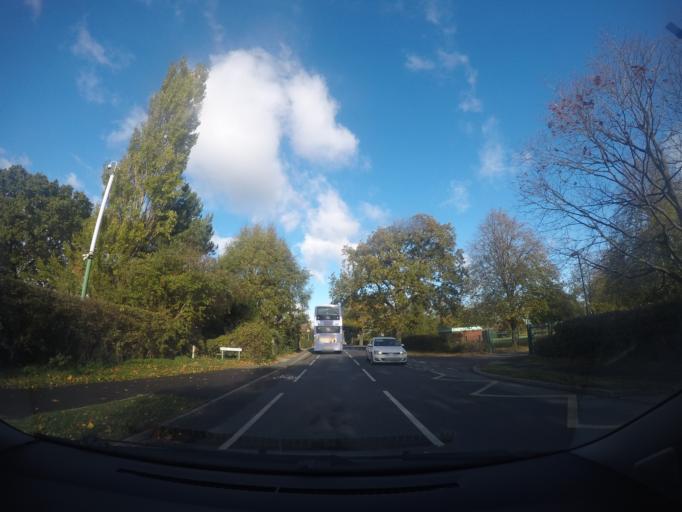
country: GB
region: England
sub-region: City of York
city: Haxby
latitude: 53.9969
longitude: -1.0719
